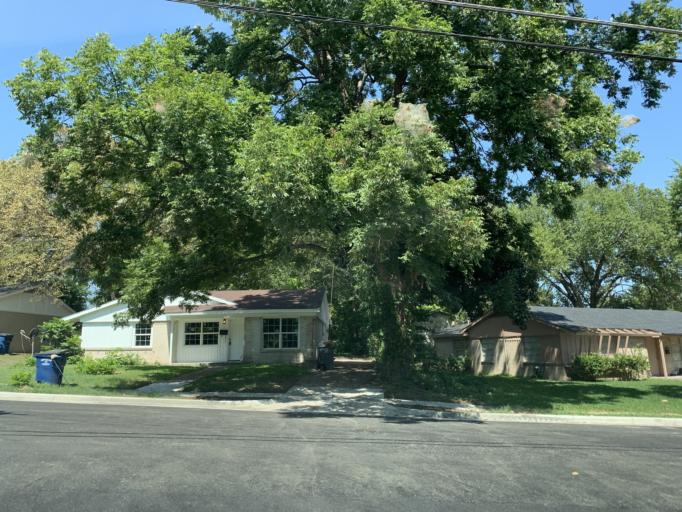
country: US
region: Texas
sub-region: Dallas County
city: Hutchins
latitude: 32.6752
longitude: -96.7546
